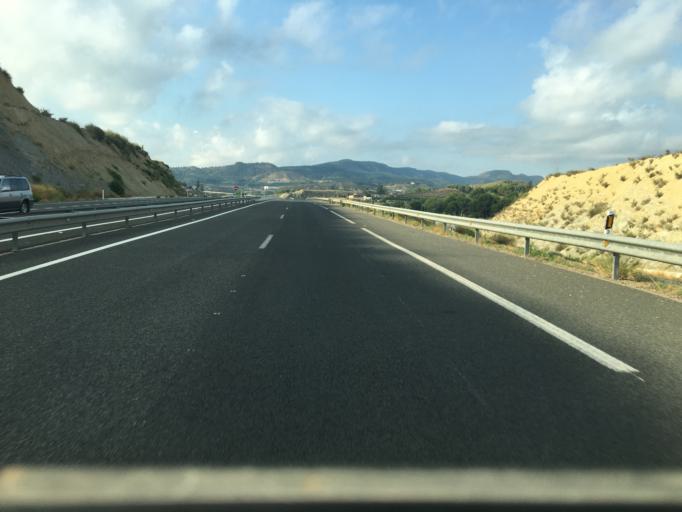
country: ES
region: Murcia
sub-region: Murcia
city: Beniel
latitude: 37.9809
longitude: -0.9748
